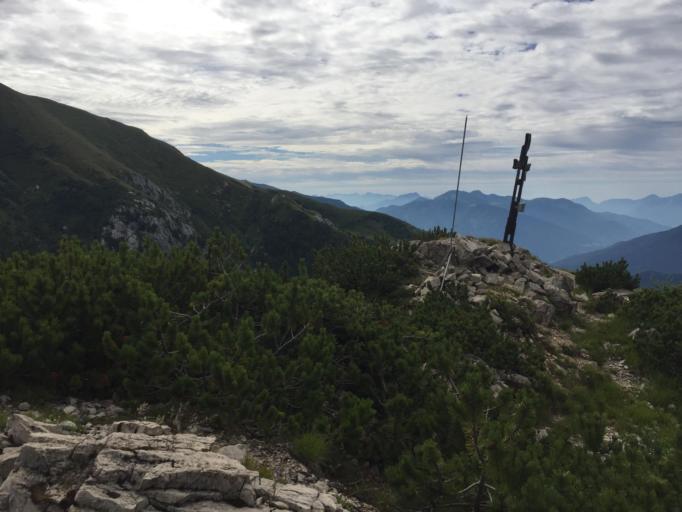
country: IT
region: Friuli Venezia Giulia
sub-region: Provincia di Udine
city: Forni Avoltri
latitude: 46.6026
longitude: 12.8006
